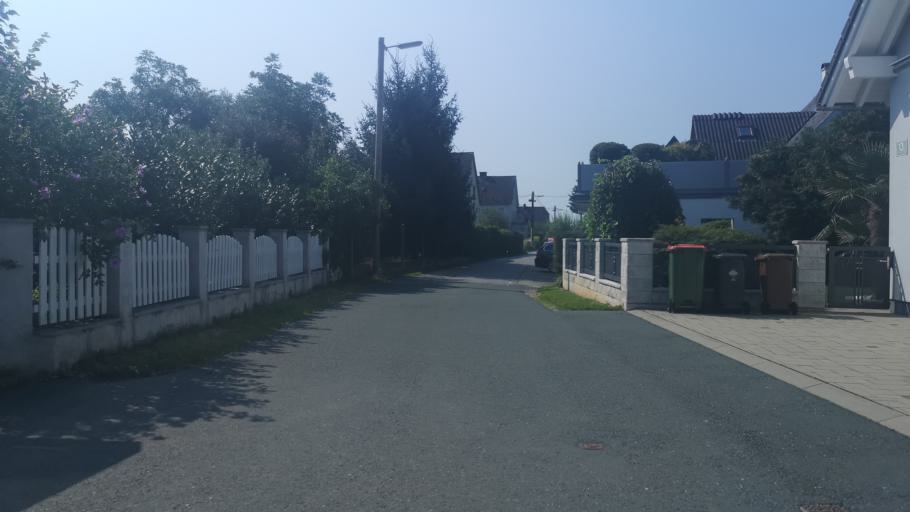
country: AT
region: Styria
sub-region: Graz Stadt
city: Wetzelsdorf
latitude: 47.0274
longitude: 15.4077
